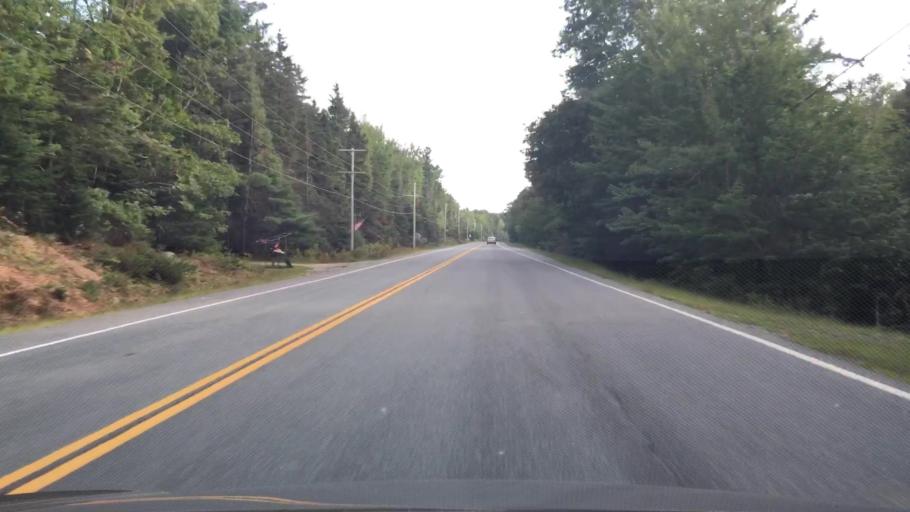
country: US
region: Maine
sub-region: Hancock County
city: Surry
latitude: 44.4885
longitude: -68.5110
